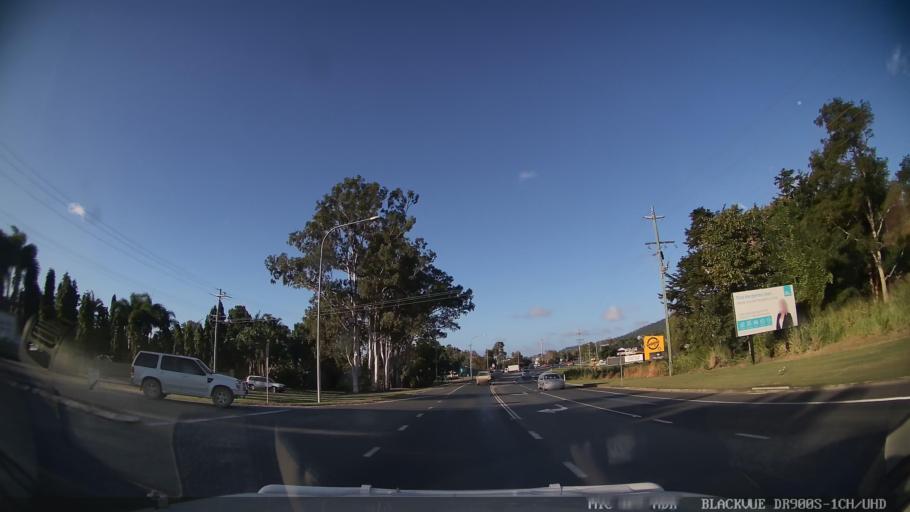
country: AU
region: Queensland
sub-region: Whitsunday
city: Proserpine
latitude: -20.2872
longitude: 148.6792
